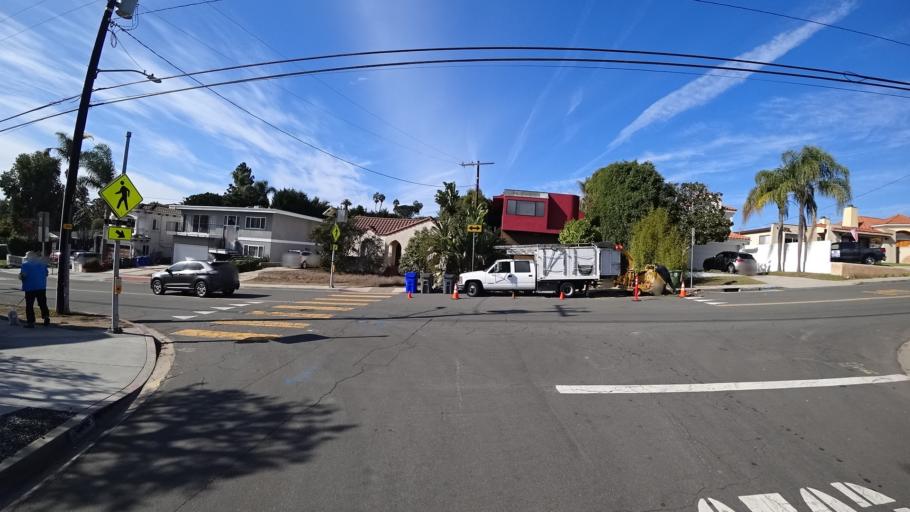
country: US
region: California
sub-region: Los Angeles County
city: Hermosa Beach
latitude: 33.8771
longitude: -118.3916
